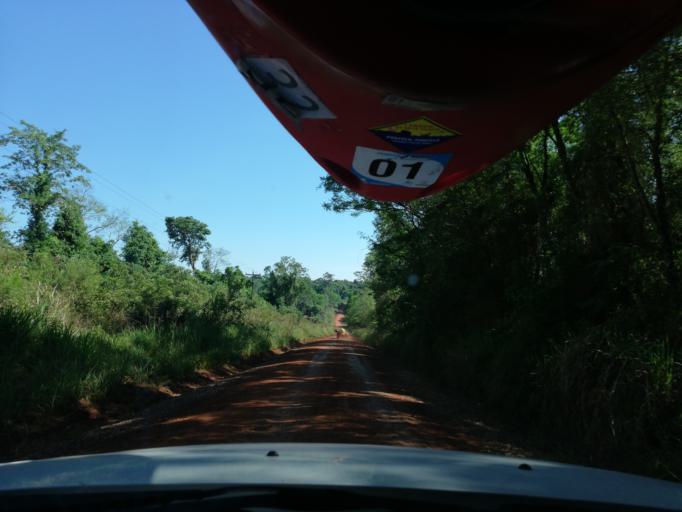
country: AR
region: Misiones
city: Puerto Leoni
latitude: -26.9730
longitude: -55.1646
